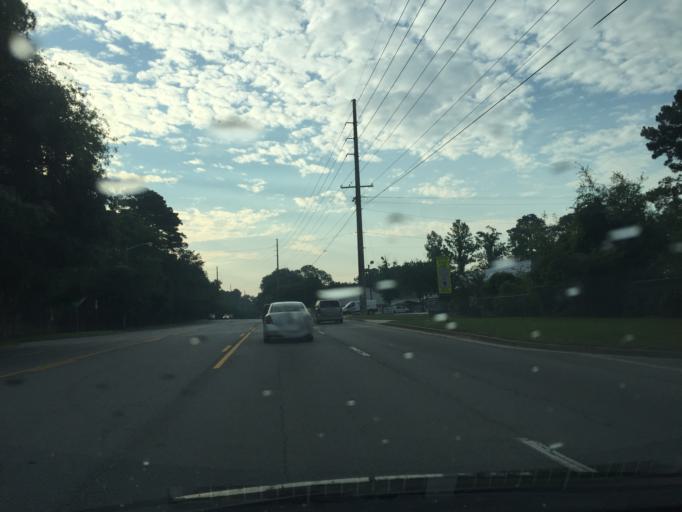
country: US
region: Georgia
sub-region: Chatham County
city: Isle of Hope
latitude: 31.9920
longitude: -81.0972
